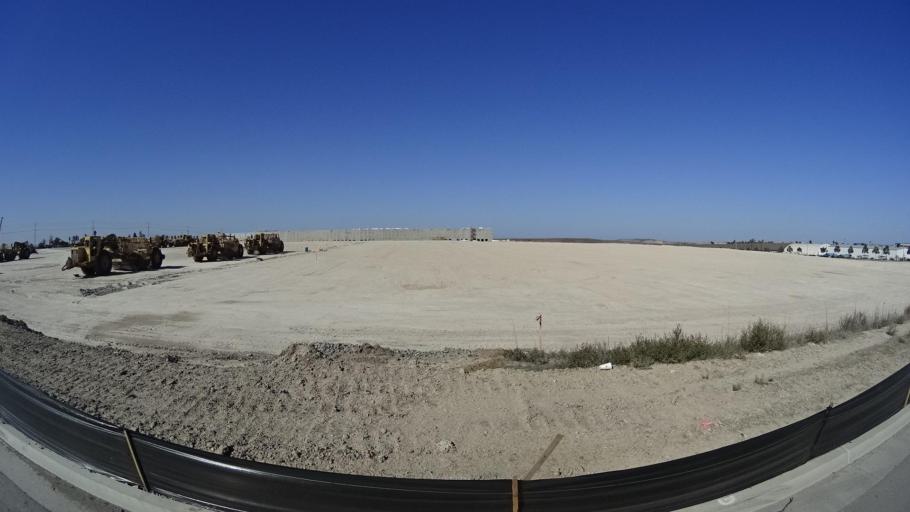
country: MX
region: Baja California
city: Tijuana
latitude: 32.5701
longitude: -116.9192
